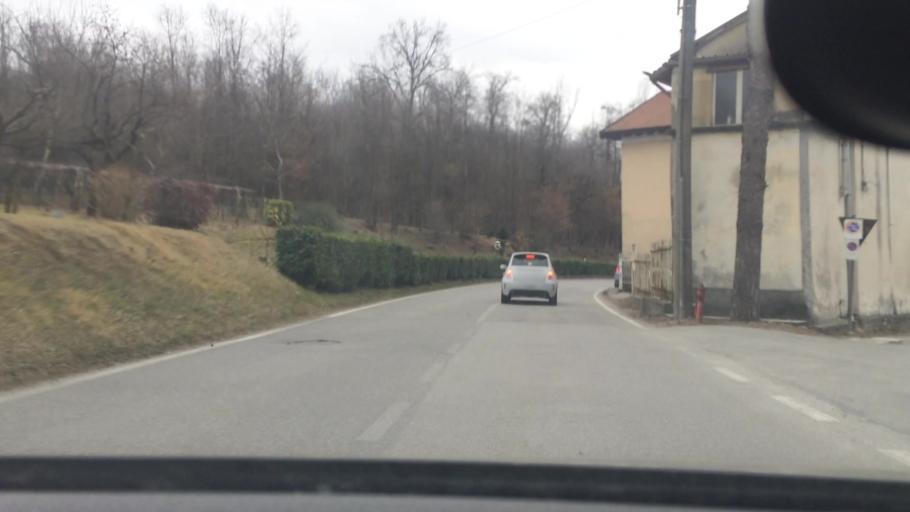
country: IT
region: Lombardy
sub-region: Provincia di Como
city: Inverigo
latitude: 45.7323
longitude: 9.2071
